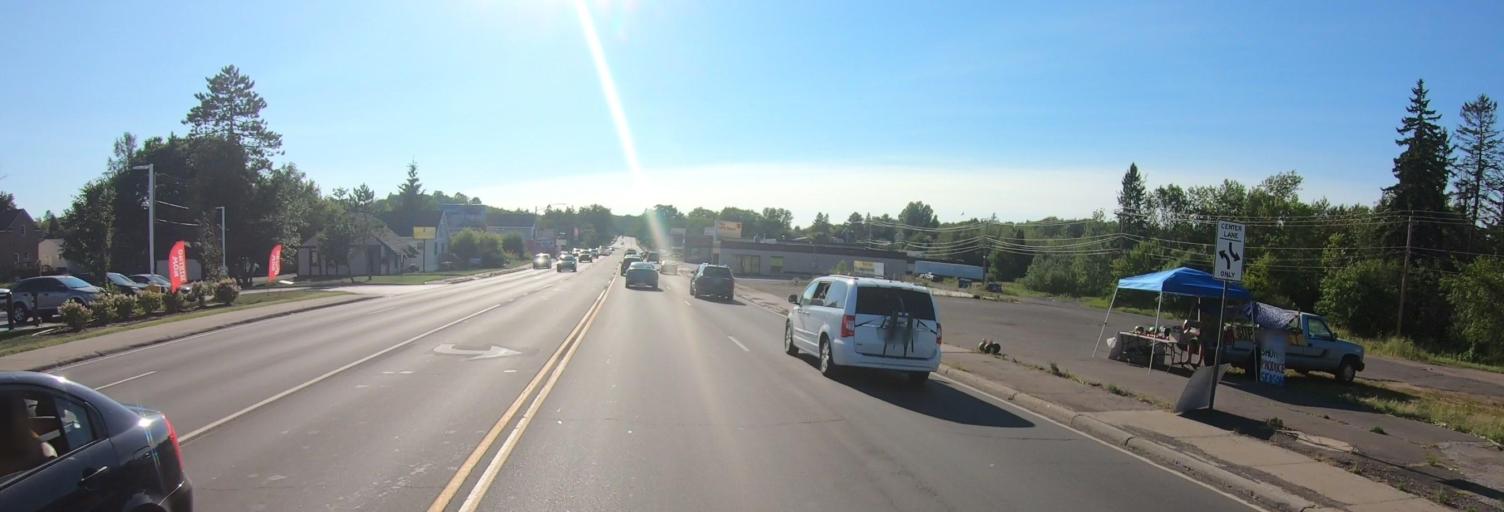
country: US
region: Minnesota
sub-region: Saint Louis County
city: Duluth
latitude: 46.8000
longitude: -92.1312
